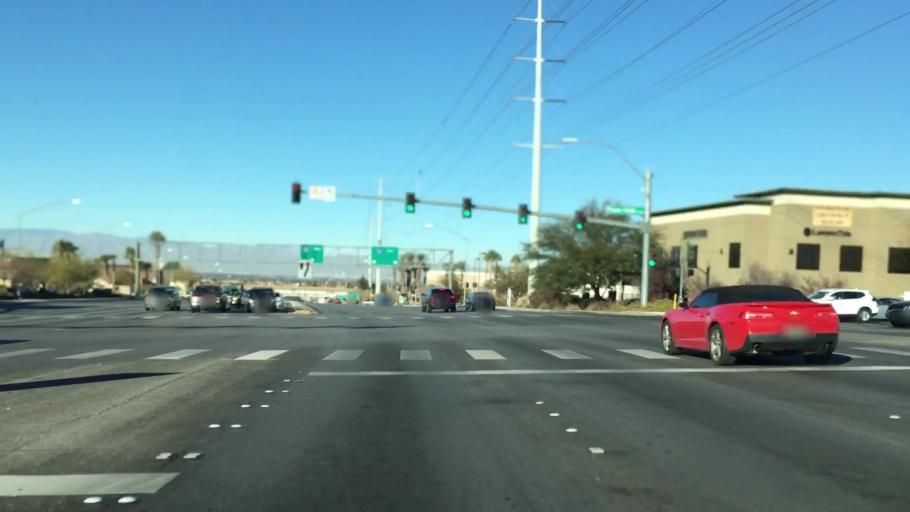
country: US
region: Nevada
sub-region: Clark County
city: Whitney
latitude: 36.0181
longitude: -115.1007
